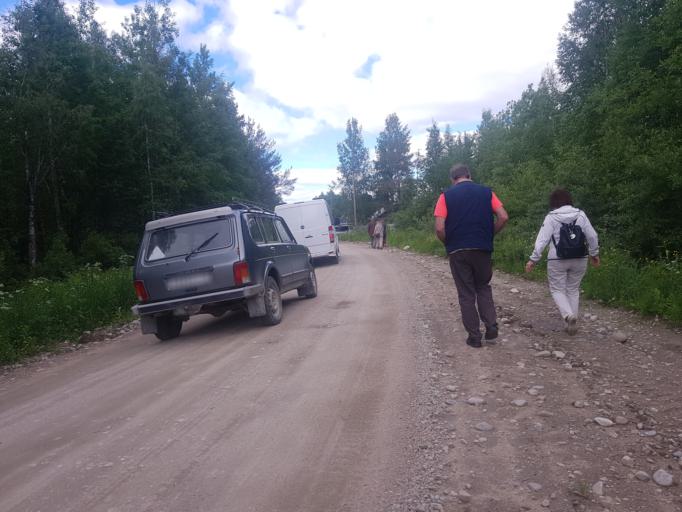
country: RU
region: Republic of Karelia
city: Kostomuksha
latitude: 65.1856
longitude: 30.2897
